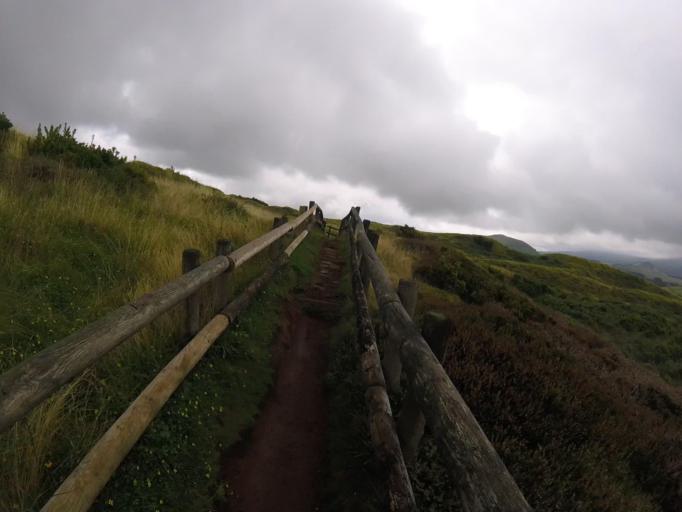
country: PT
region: Azores
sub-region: Praia da Vitoria
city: Biscoitos
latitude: 38.7292
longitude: -27.2322
